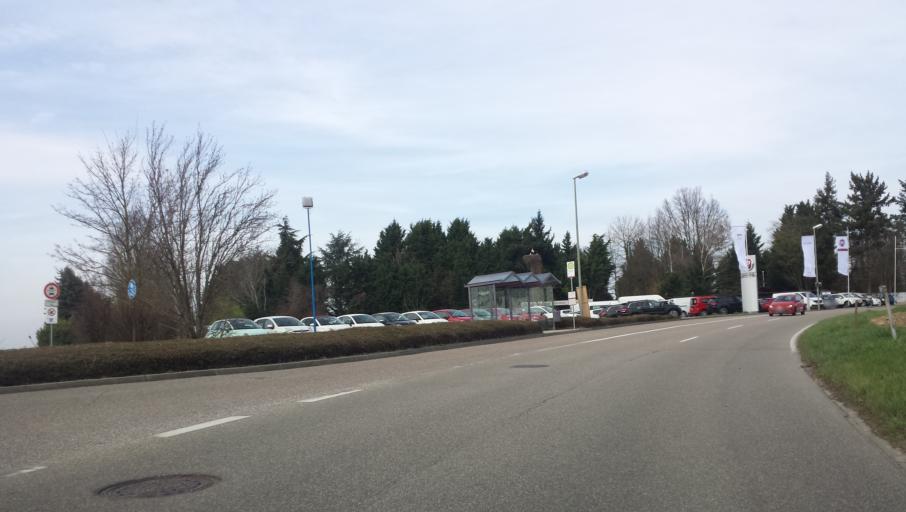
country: DE
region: Rheinland-Pfalz
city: Dudenhofen
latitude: 49.2731
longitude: 8.4014
